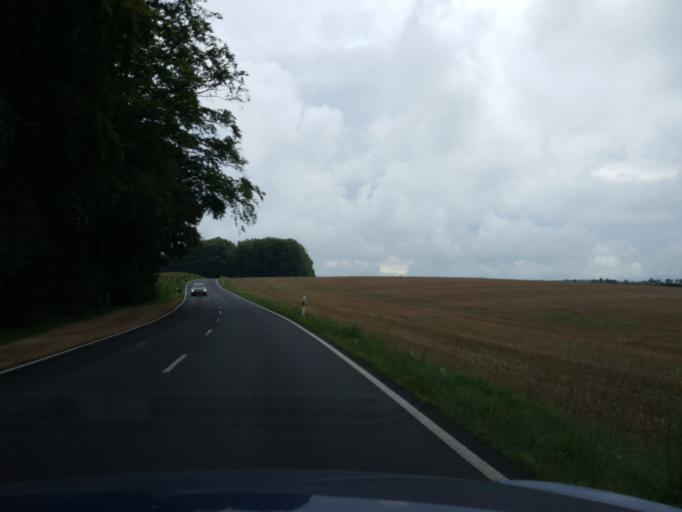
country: LU
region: Luxembourg
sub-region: Canton de Capellen
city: Kopstal
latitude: 49.7100
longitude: 6.0794
